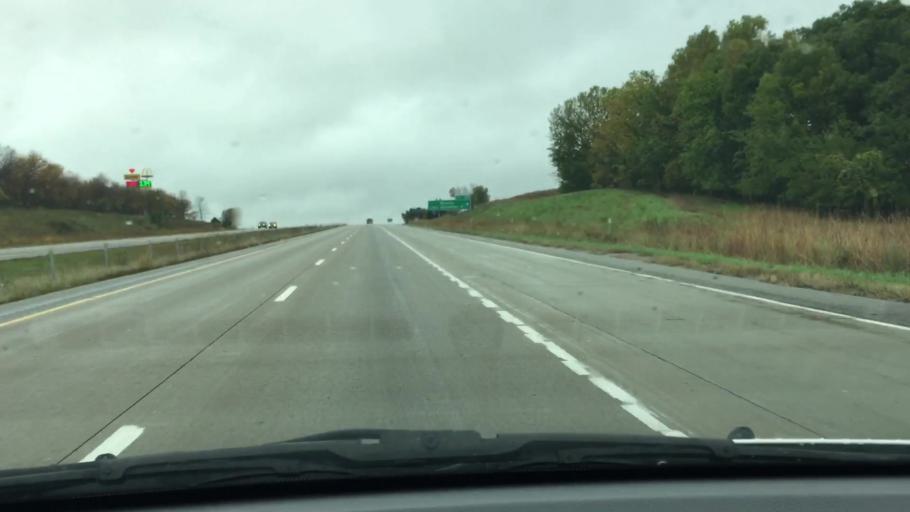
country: US
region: Iowa
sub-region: Jasper County
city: Newton
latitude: 41.6823
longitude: -92.9904
